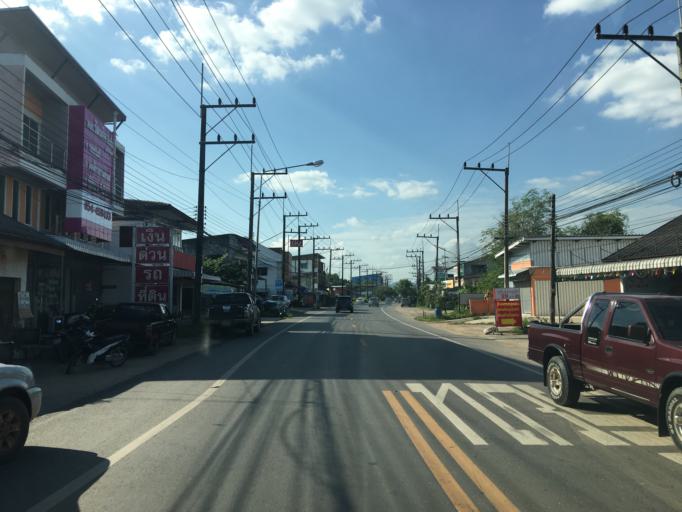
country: TH
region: Phayao
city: Chun
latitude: 19.3419
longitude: 100.1225
